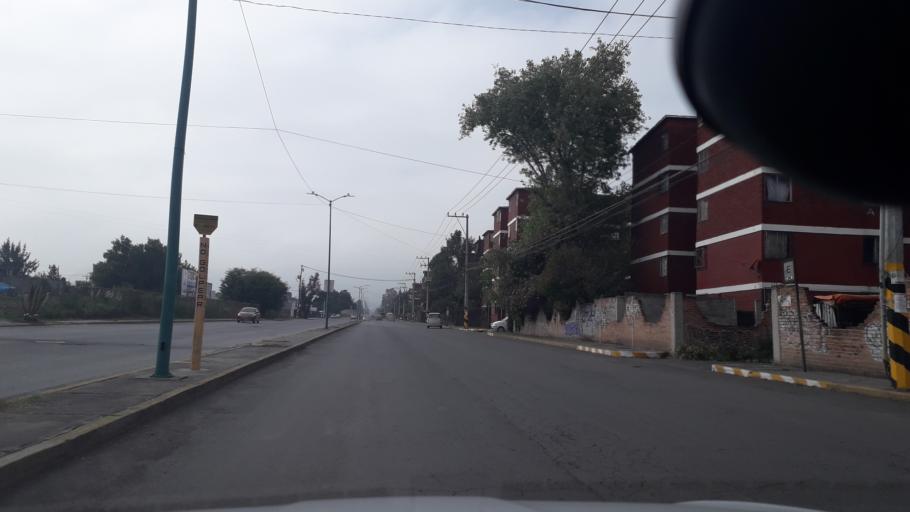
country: MX
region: Mexico
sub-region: Jaltenco
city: Alborada Jaltenco
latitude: 19.6560
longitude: -99.0762
